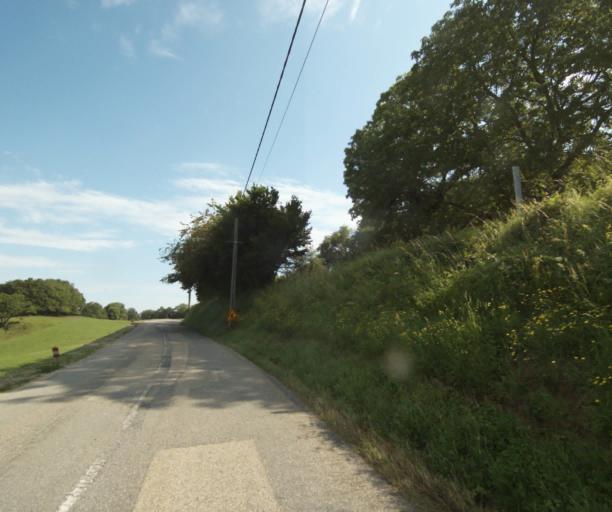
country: FR
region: Rhone-Alpes
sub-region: Departement de la Haute-Savoie
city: Lyaud
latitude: 46.3286
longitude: 6.5087
